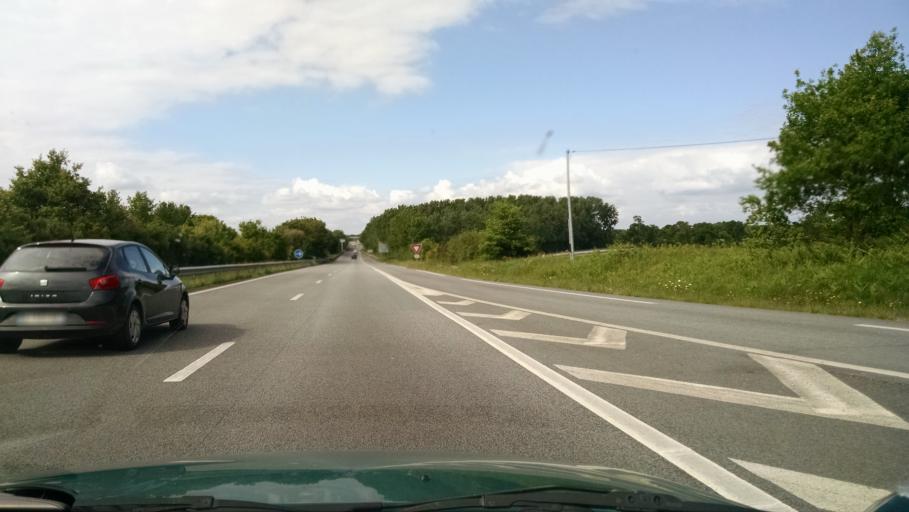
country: FR
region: Brittany
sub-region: Departement d'Ille-et-Vilaine
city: Grand-Fougeray
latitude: 47.6971
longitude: -1.7031
